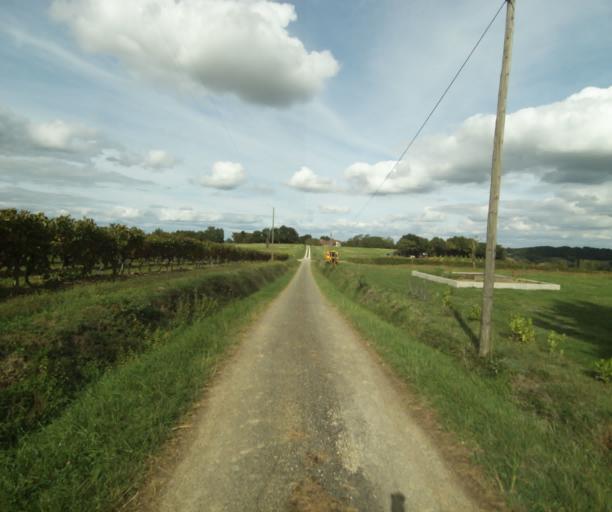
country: FR
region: Midi-Pyrenees
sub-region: Departement du Gers
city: Eauze
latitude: 43.8561
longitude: 0.1528
